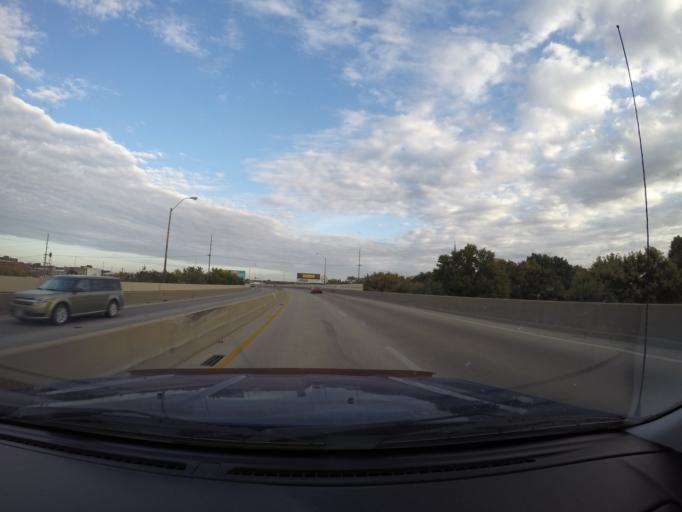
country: US
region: Kansas
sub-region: Shawnee County
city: Topeka
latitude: 39.0587
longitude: -95.6758
